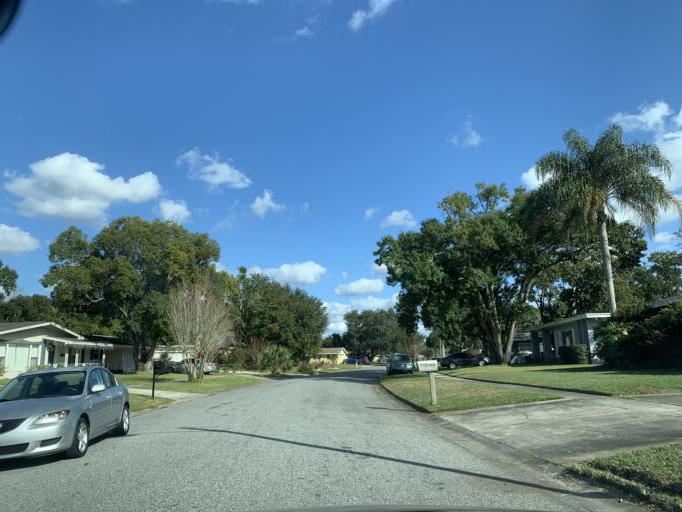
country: US
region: Florida
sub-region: Orange County
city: Eatonville
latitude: 28.6121
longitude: -81.4022
